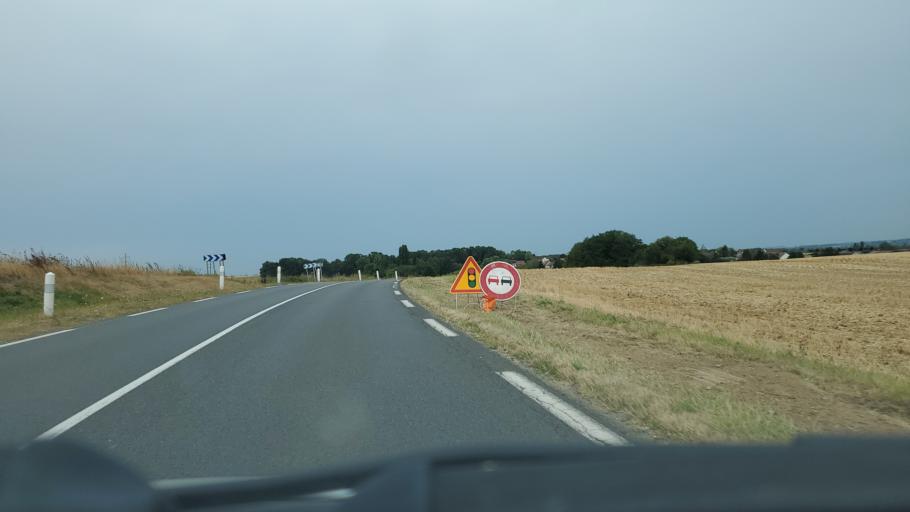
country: FR
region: Ile-de-France
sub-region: Departement de Seine-et-Marne
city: Chailly-en-Brie
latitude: 48.7873
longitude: 3.1330
